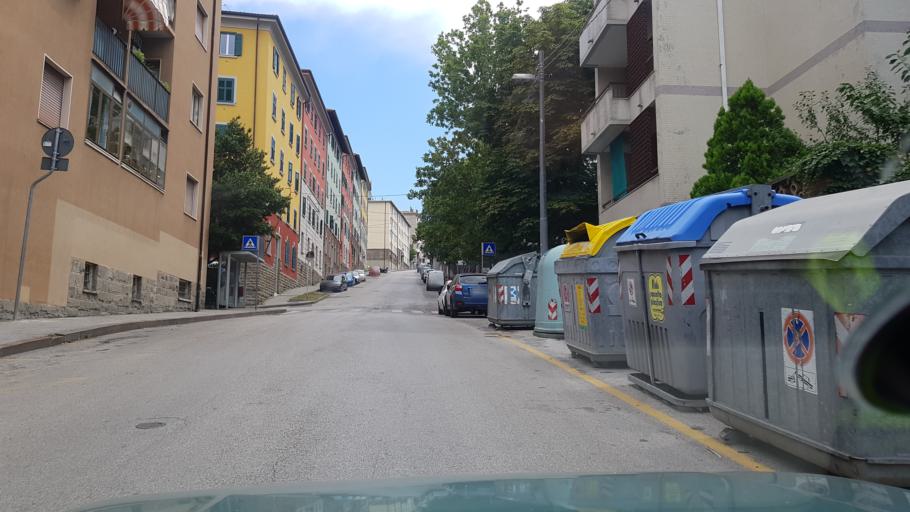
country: IT
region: Friuli Venezia Giulia
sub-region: Provincia di Trieste
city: Trieste
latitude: 45.6536
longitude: 13.8046
